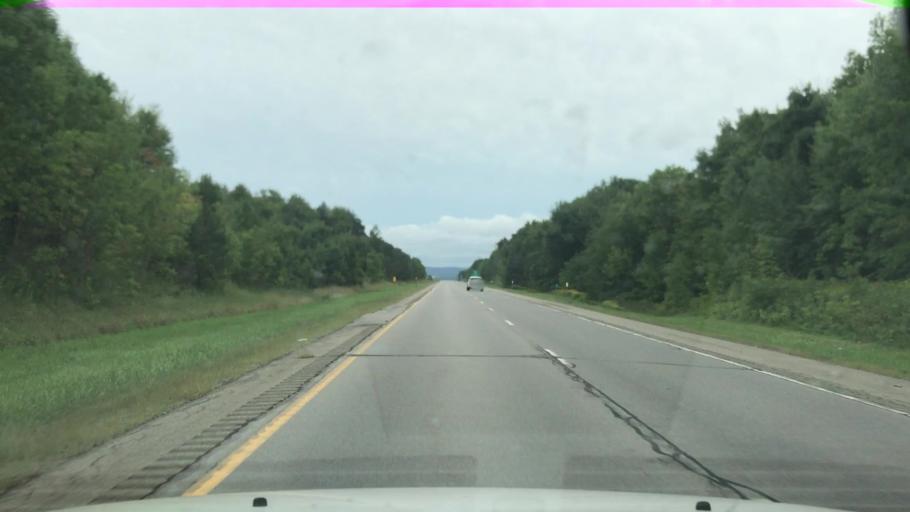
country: US
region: New York
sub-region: Erie County
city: Springville
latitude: 42.5321
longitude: -78.7046
